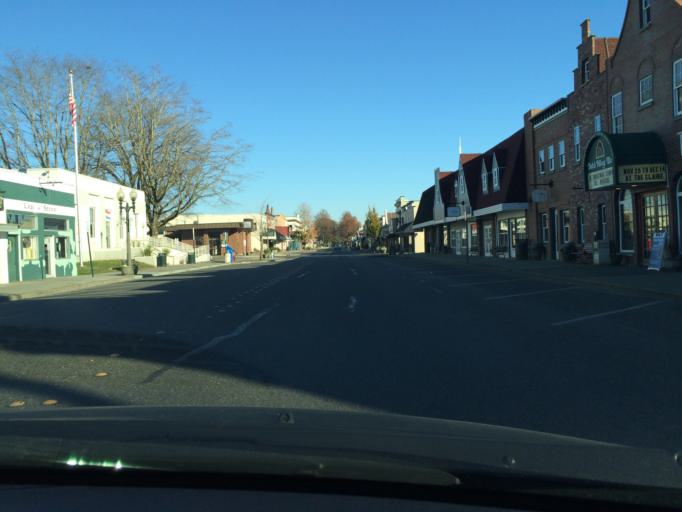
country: US
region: Washington
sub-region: Whatcom County
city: Lynden
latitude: 48.9421
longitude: -122.4554
